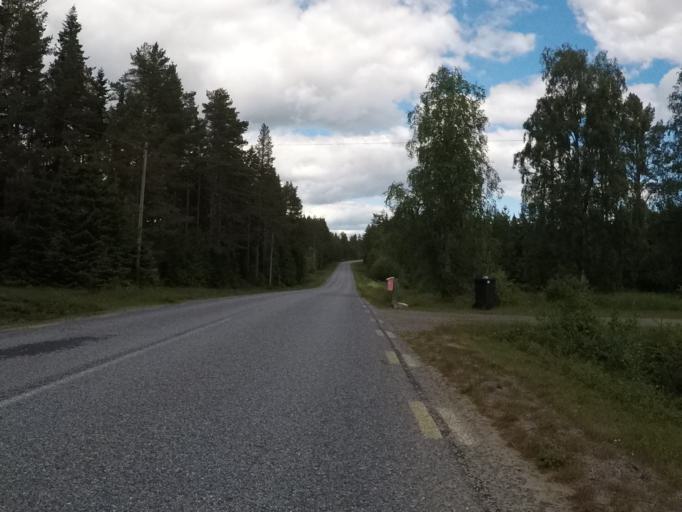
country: SE
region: Vaesterbotten
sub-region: Umea Kommun
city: Saevar
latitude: 63.9495
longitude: 20.7923
